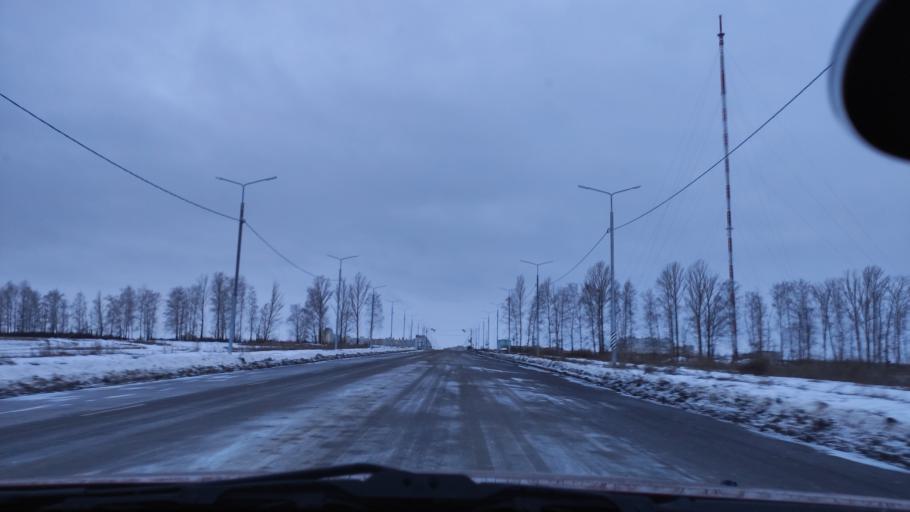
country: RU
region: Tambov
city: Donskoye
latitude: 52.7818
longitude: 41.4250
